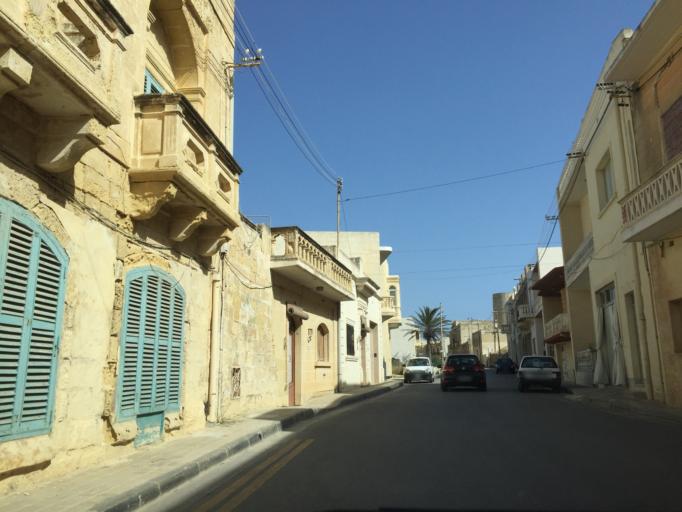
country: MT
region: L-Gharb
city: Gharb
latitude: 36.0584
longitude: 14.2107
